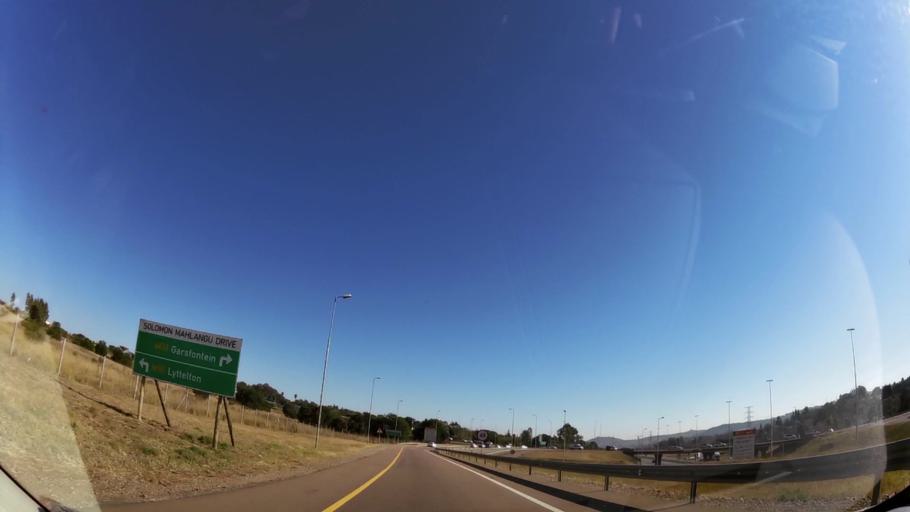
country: ZA
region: Gauteng
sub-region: City of Tshwane Metropolitan Municipality
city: Centurion
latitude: -25.8157
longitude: 28.2348
